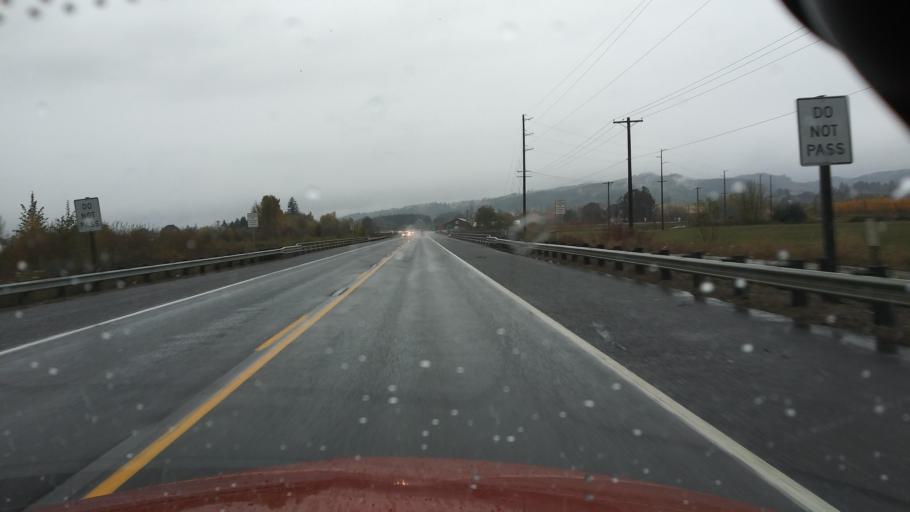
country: US
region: Oregon
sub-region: Washington County
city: Forest Grove
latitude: 45.5057
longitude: -123.1112
